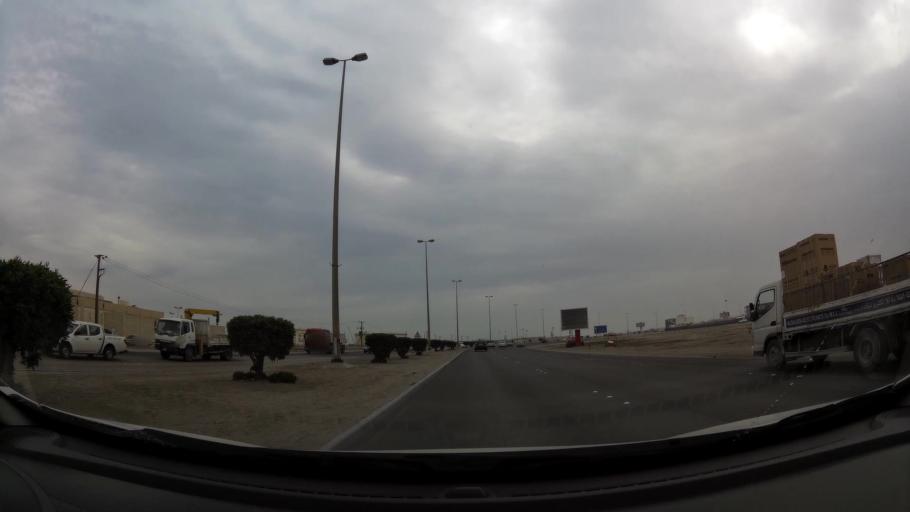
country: BH
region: Northern
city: Sitrah
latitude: 26.1466
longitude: 50.6189
